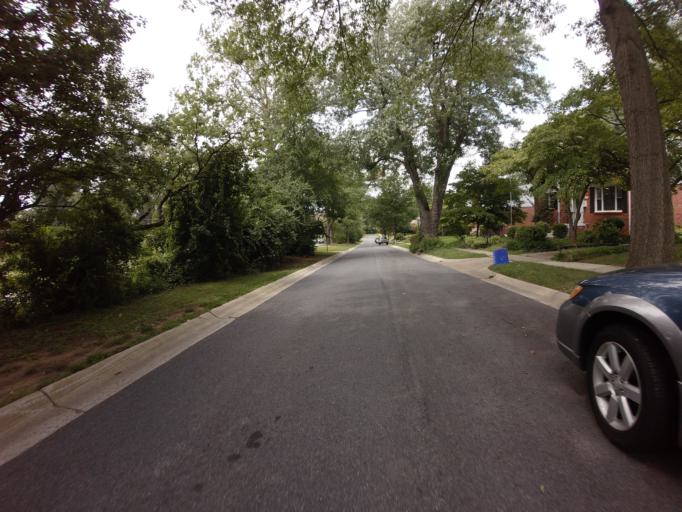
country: US
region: Maryland
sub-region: Montgomery County
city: North Bethesda
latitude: 39.0348
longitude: -77.1003
